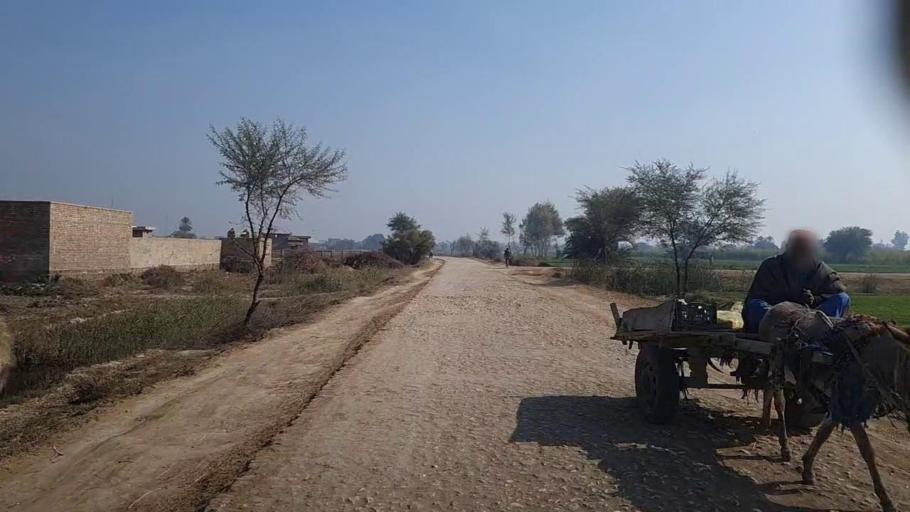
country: PK
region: Sindh
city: Khairpur
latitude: 27.9438
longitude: 69.6589
